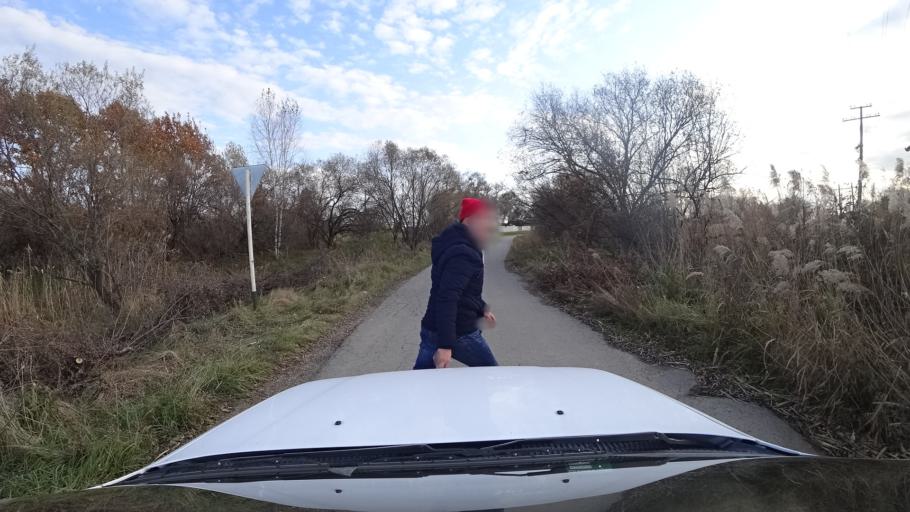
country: RU
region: Primorskiy
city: Lazo
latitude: 45.8232
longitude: 133.6147
